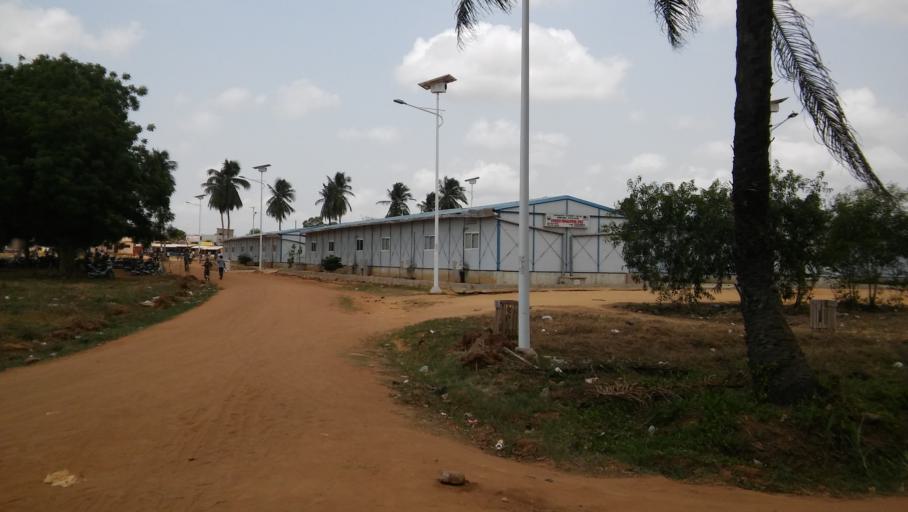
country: BJ
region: Atlantique
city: Abomey-Calavi
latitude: 6.4214
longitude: 2.3410
